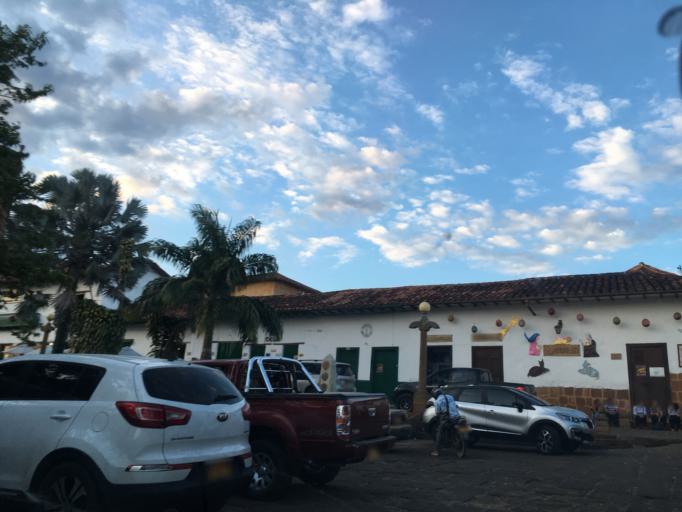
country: CO
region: Santander
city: Barichara
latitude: 6.6360
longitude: -73.2230
